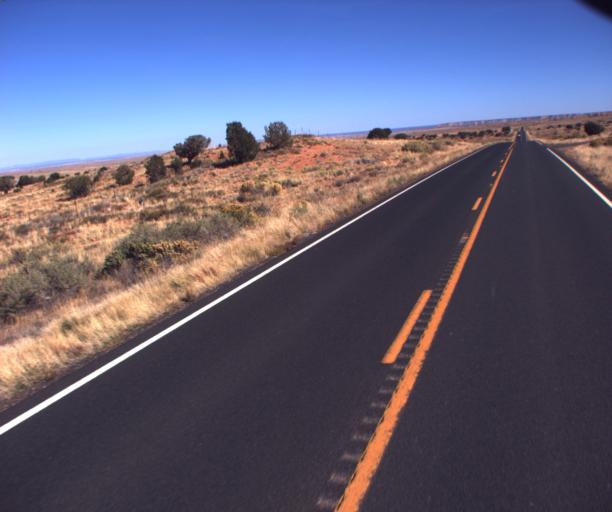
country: US
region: Arizona
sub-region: Apache County
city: Ganado
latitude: 35.7851
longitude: -109.7039
